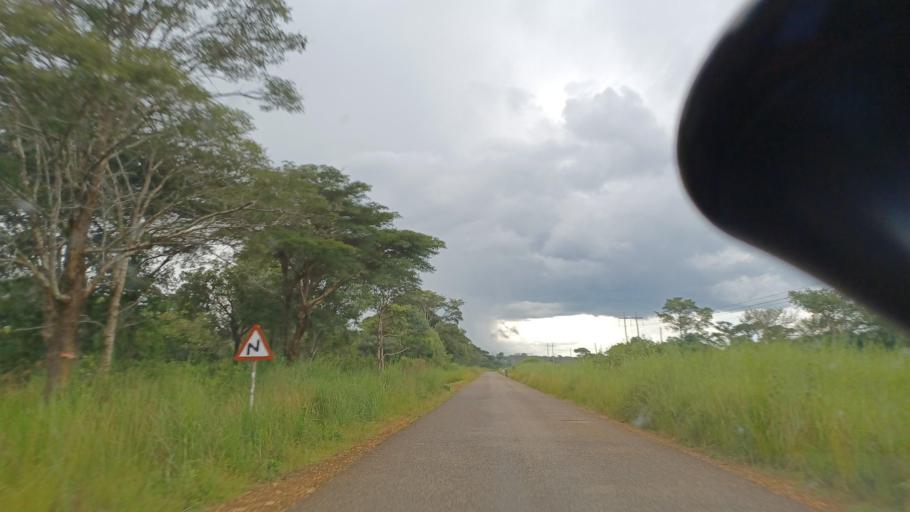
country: ZM
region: North-Western
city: Kasempa
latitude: -13.0065
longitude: 26.0097
